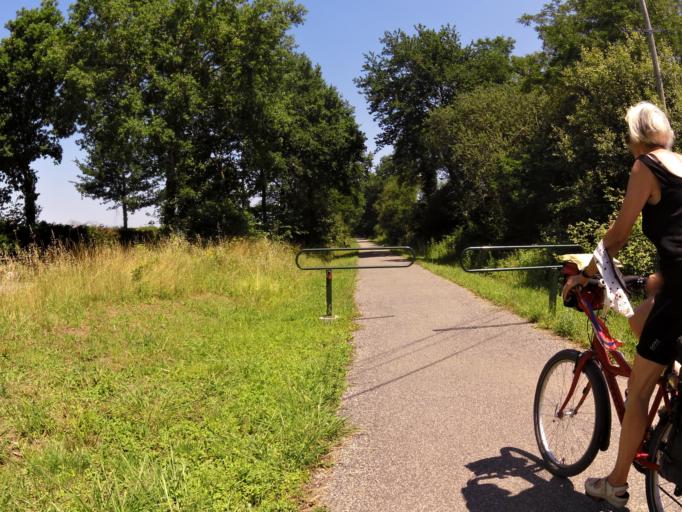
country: FR
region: Aquitaine
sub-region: Departement des Pyrenees-Atlantiques
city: Salies-de-Bearn
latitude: 43.4670
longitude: -0.9456
